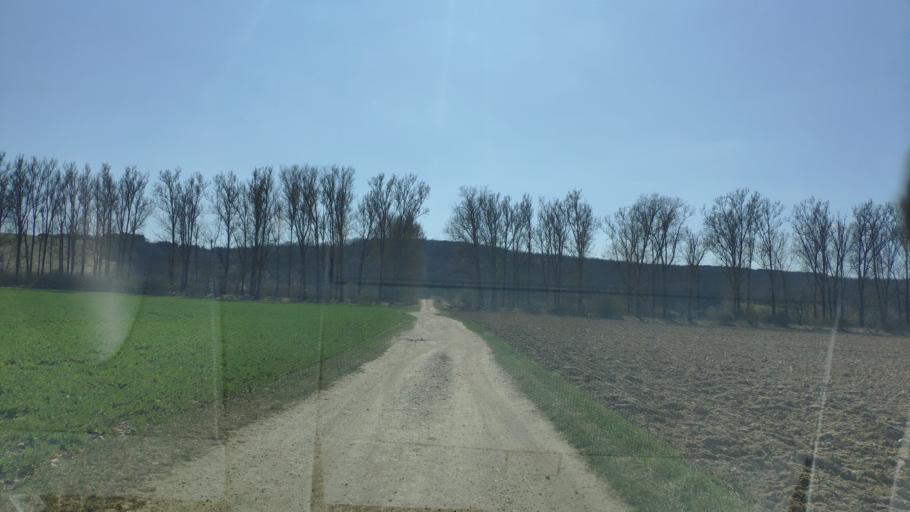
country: SK
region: Kosicky
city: Moldava nad Bodvou
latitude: 48.5704
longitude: 20.9453
